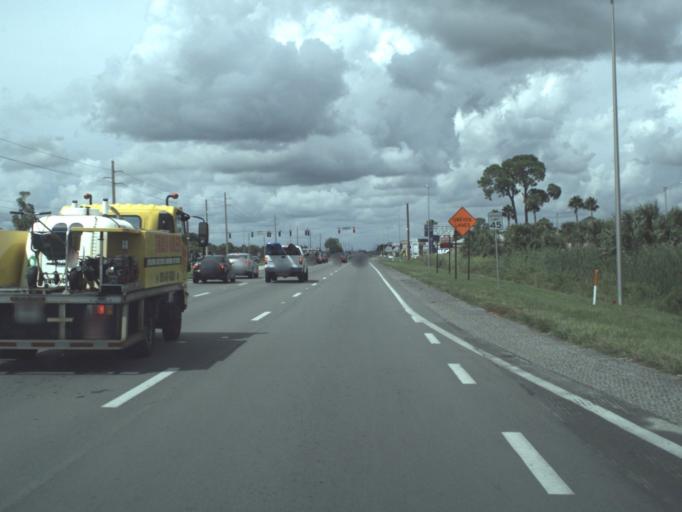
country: US
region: Florida
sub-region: Charlotte County
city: Port Charlotte
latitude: 26.9867
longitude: -82.1050
